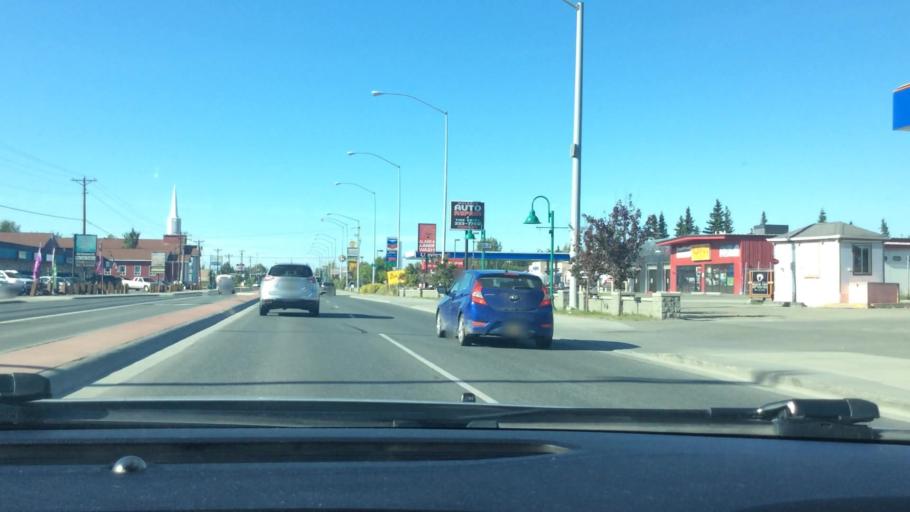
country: US
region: Alaska
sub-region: Anchorage Municipality
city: Elmendorf Air Force Base
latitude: 61.2170
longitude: -149.7334
